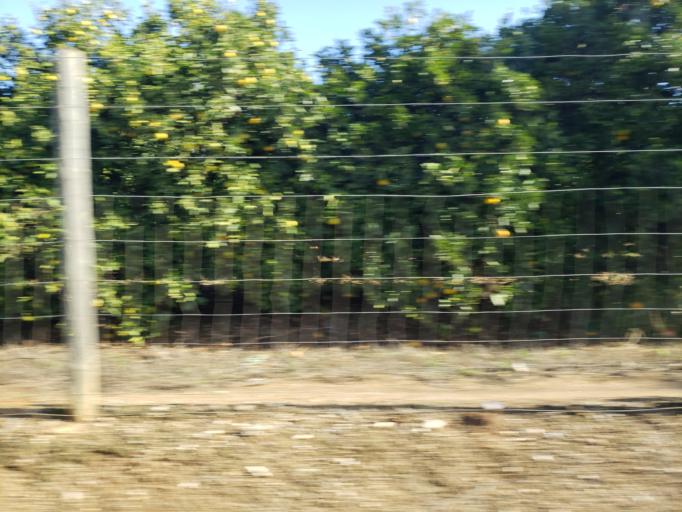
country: PT
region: Faro
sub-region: Portimao
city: Alvor
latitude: 37.1681
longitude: -8.5788
